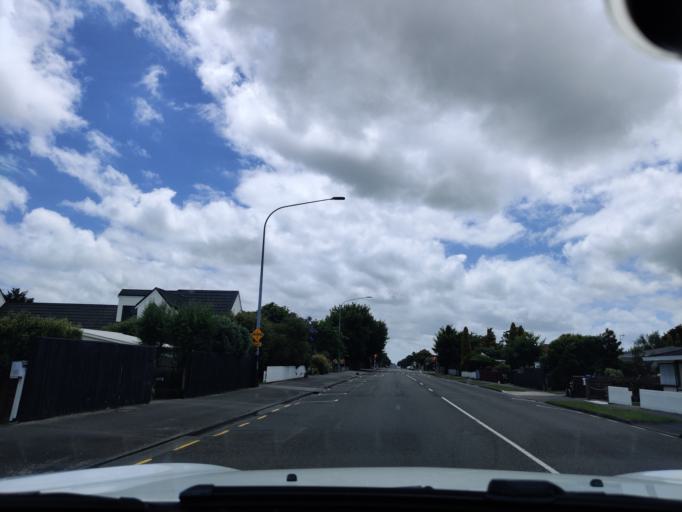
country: NZ
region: Manawatu-Wanganui
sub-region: Palmerston North City
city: Palmerston North
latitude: -40.3617
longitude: 175.6329
